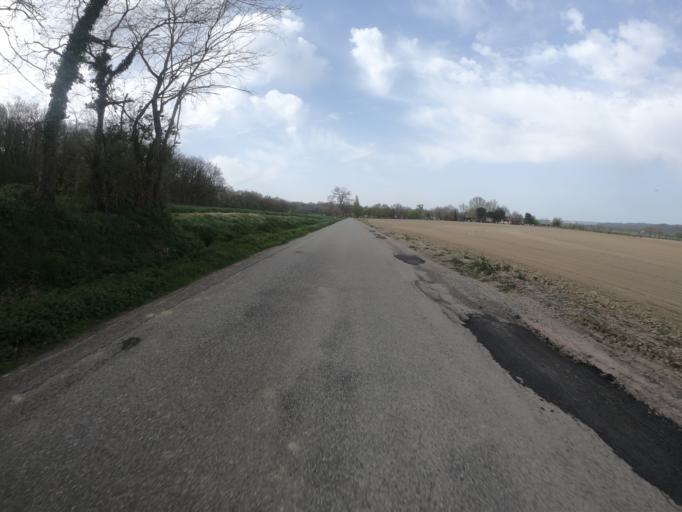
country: FR
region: Midi-Pyrenees
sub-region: Departement de l'Ariege
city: La Tour-du-Crieu
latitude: 43.1278
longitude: 1.7187
